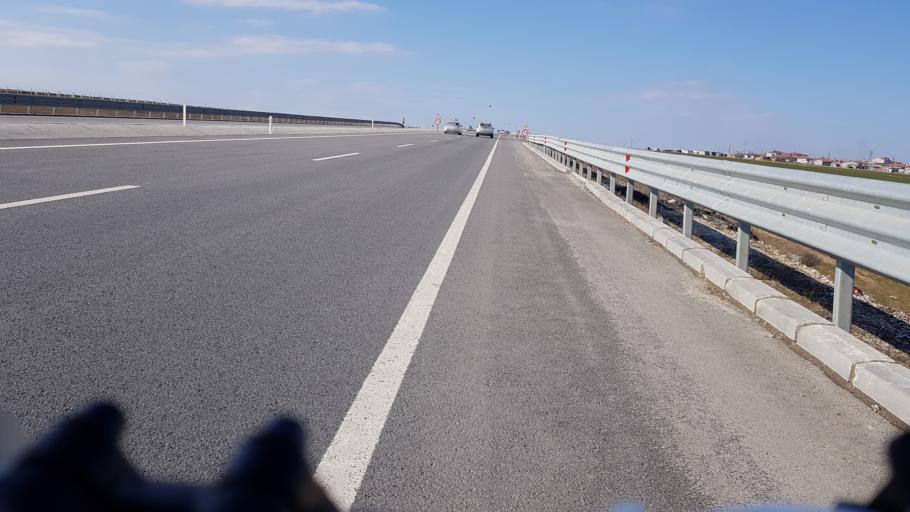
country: TR
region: Tekirdag
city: Saray
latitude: 41.4277
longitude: 27.9114
